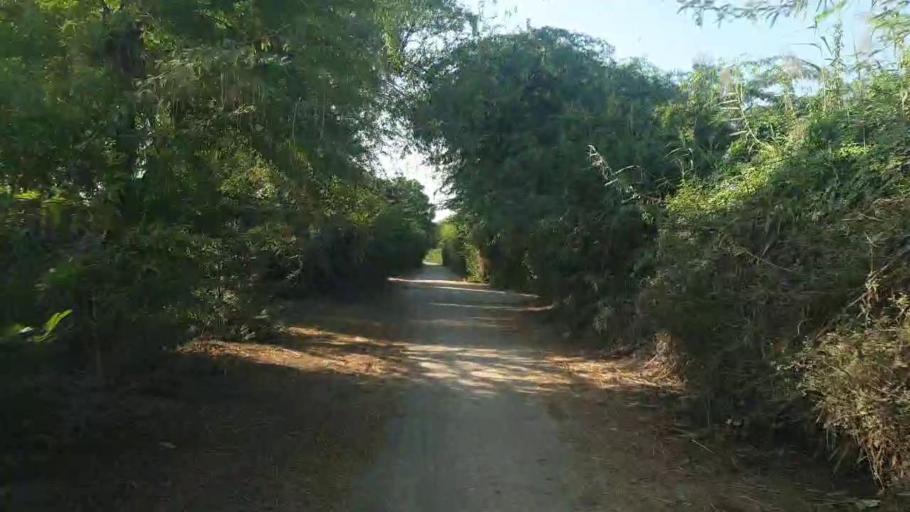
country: PK
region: Sindh
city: Tando Bago
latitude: 24.7438
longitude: 68.9314
